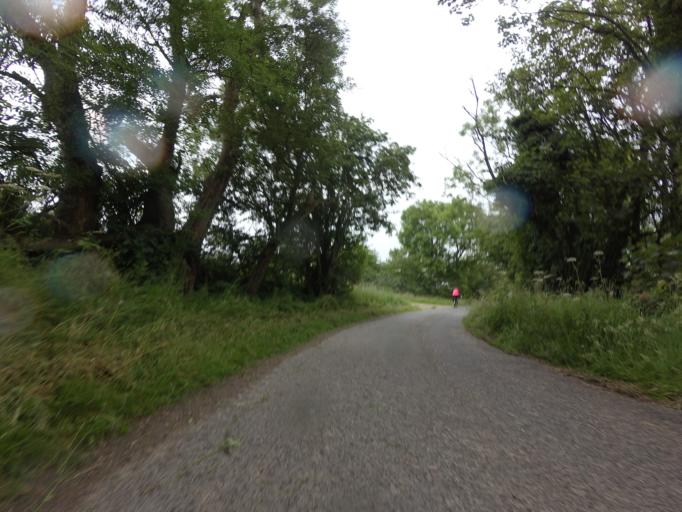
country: GB
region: Scotland
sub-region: Moray
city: Cullen
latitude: 57.6713
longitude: -2.7783
